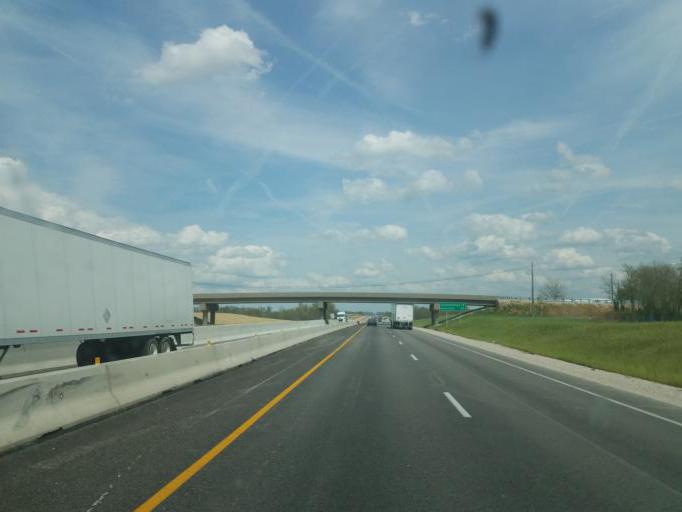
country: US
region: Kentucky
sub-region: Larue County
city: Hodgenville
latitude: 37.5376
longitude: -85.8813
